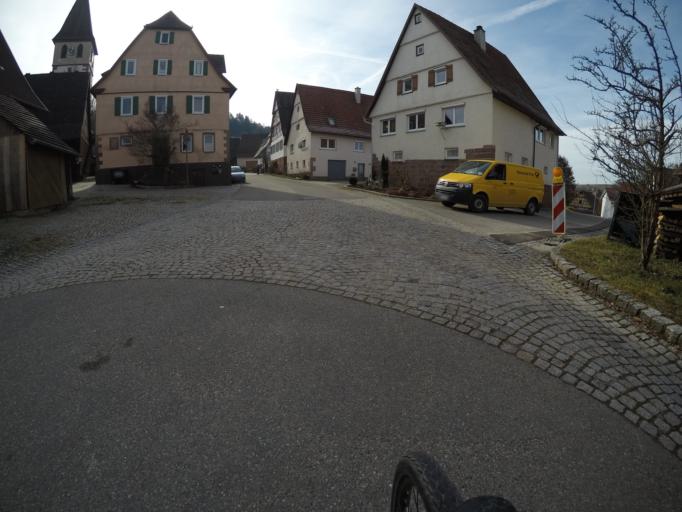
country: DE
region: Baden-Wuerttemberg
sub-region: Karlsruhe Region
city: Wildberg
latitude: 48.6487
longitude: 8.7759
